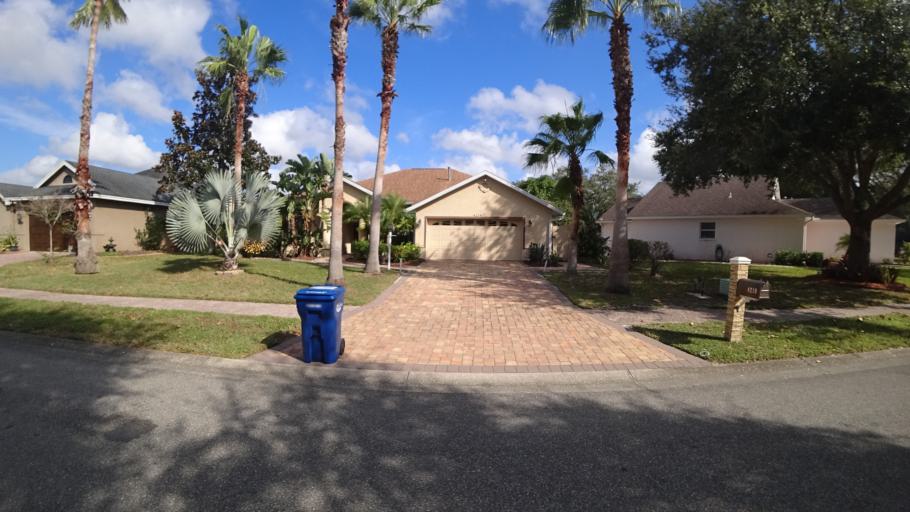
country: US
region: Florida
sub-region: Sarasota County
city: North Sarasota
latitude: 27.4088
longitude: -82.5087
